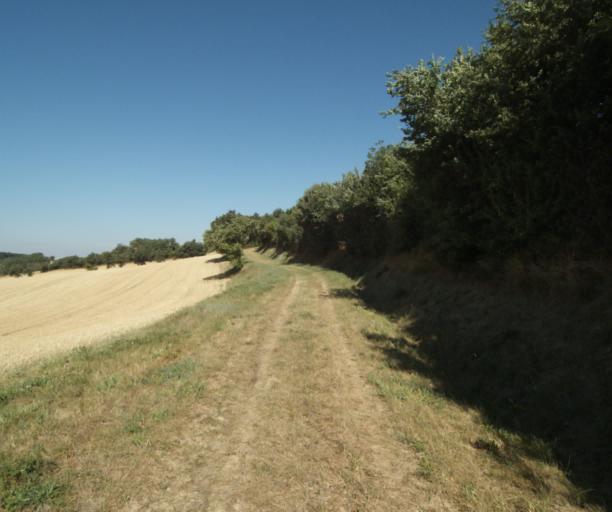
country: FR
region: Midi-Pyrenees
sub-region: Departement de la Haute-Garonne
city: Saint-Felix-Lauragais
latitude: 43.4992
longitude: 1.9363
